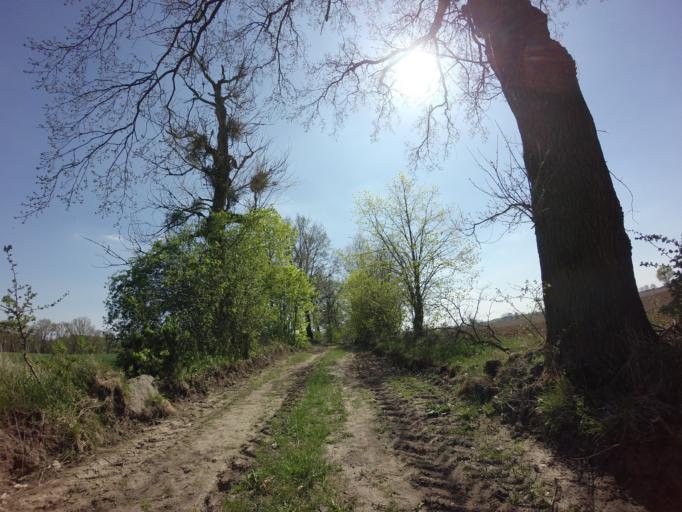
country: PL
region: West Pomeranian Voivodeship
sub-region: Powiat stargardzki
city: Suchan
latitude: 53.1925
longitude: 15.3139
